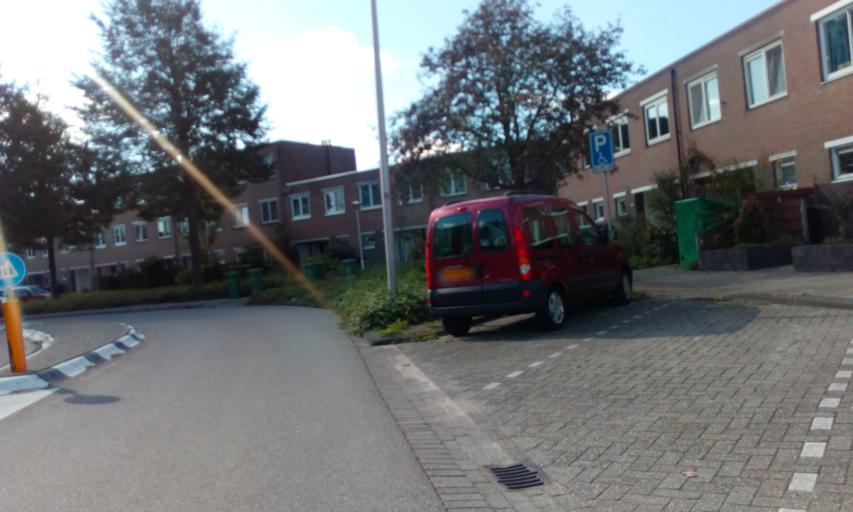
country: NL
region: South Holland
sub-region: Gemeente Zoetermeer
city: Zoetermeer
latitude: 52.0759
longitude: 4.5137
